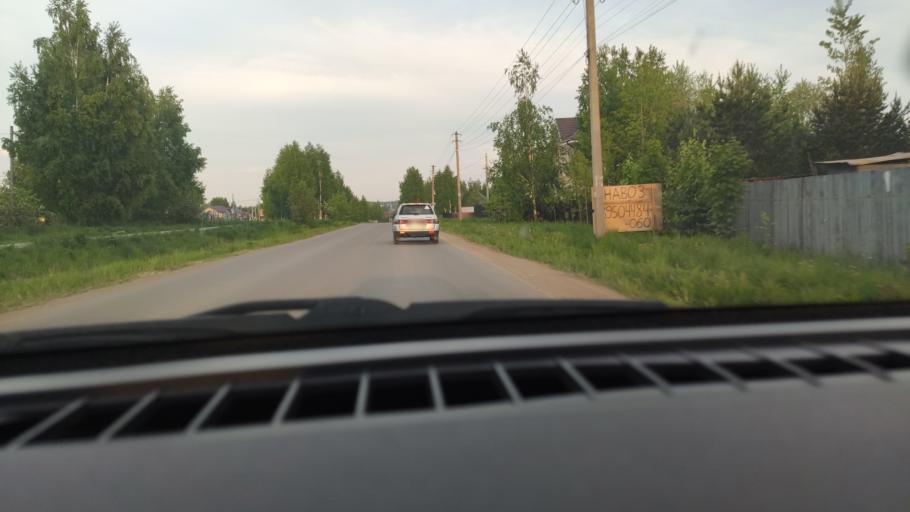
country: RU
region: Perm
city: Kondratovo
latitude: 58.0570
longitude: 56.0095
